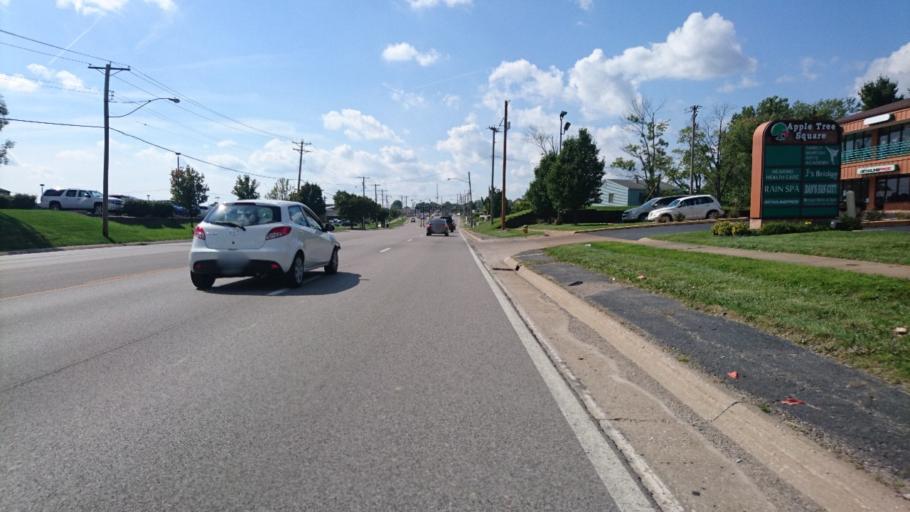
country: US
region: Missouri
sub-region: Saint Louis County
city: Ellisville
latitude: 38.5928
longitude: -90.5816
